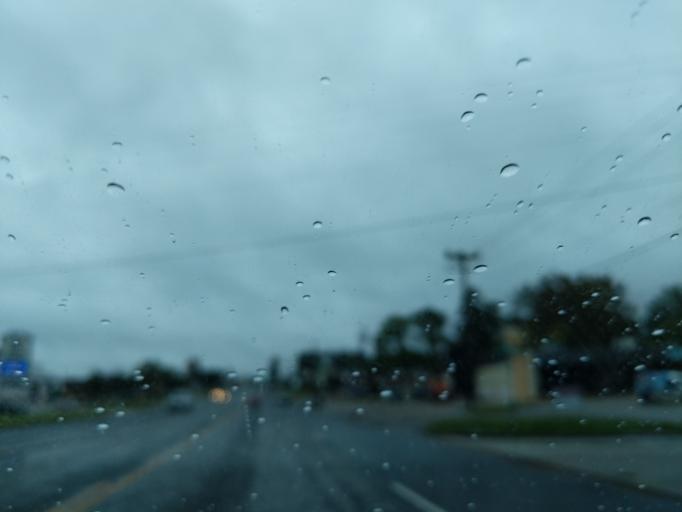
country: US
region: Texas
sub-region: Nacogdoches County
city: Nacogdoches
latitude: 31.6350
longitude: -94.6530
